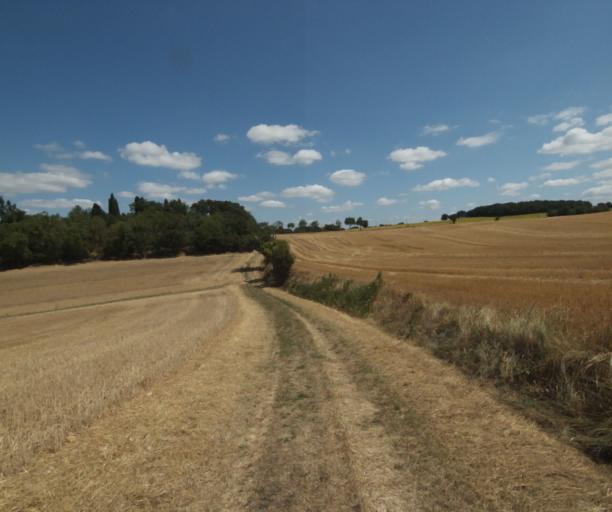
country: FR
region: Midi-Pyrenees
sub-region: Departement de la Haute-Garonne
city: Saint-Felix-Lauragais
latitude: 43.4726
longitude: 1.8606
